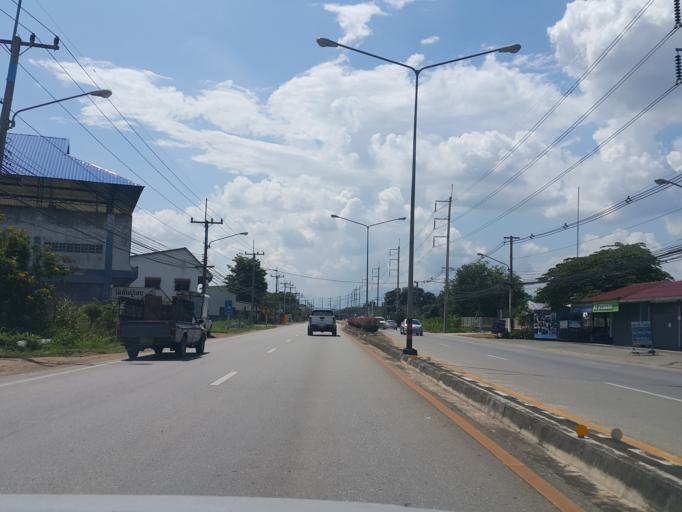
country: TH
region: Chiang Mai
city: Mae Taeng
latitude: 19.1116
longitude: 98.9388
